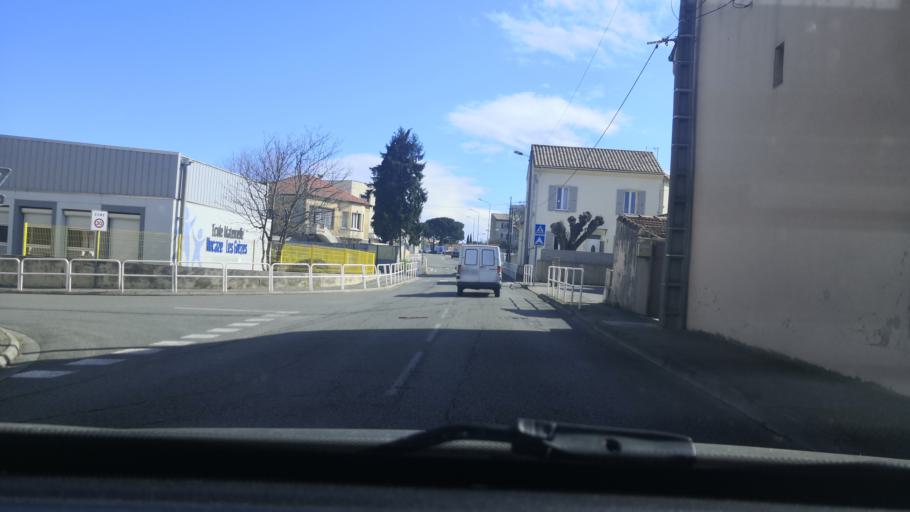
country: FR
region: Rhone-Alpes
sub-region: Departement de la Drome
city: Montelimar
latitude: 44.5490
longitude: 4.7447
